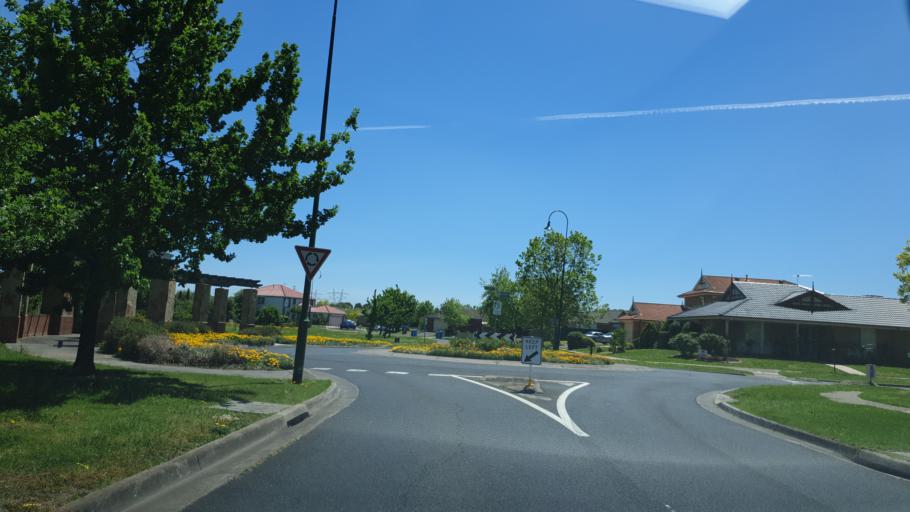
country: AU
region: Victoria
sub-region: Casey
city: Narre Warren South
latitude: -38.0612
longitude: 145.2858
